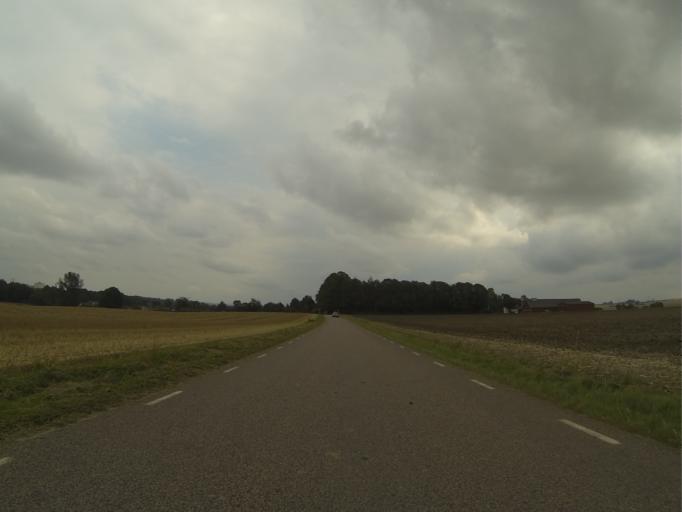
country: SE
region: Skane
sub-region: Lunds Kommun
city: Lund
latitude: 55.7759
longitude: 13.2227
